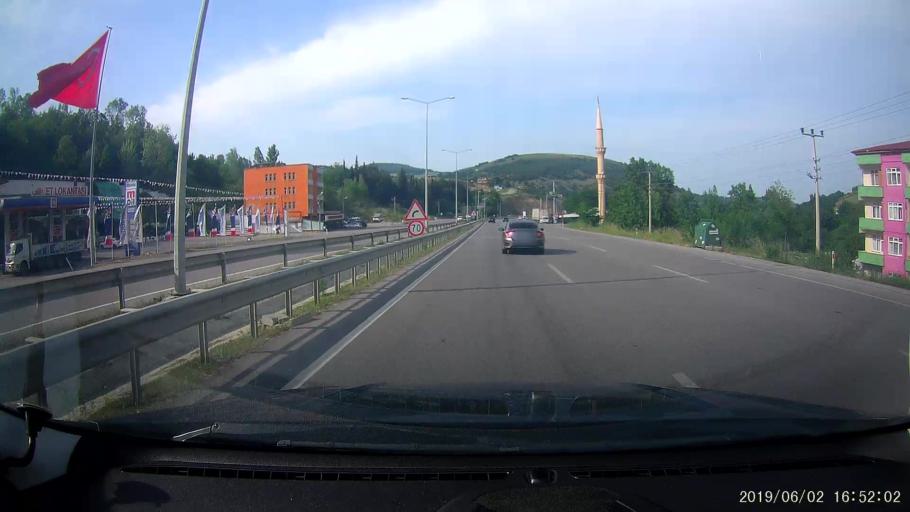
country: TR
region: Samsun
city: Samsun
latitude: 41.2820
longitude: 36.1914
